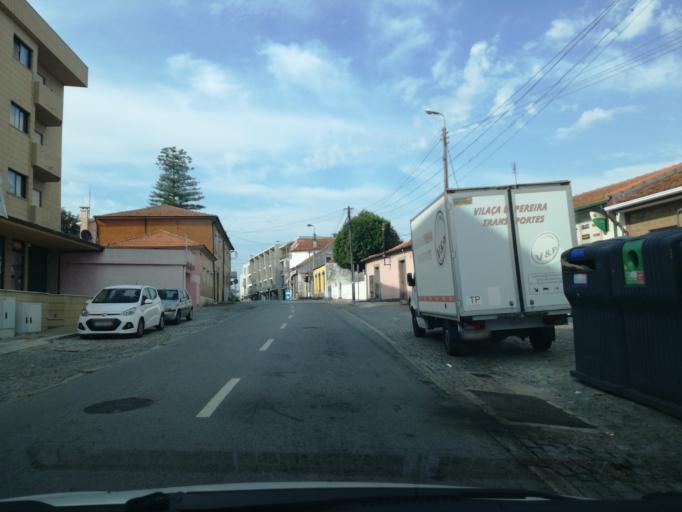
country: PT
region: Porto
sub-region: Vila Nova de Gaia
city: Sao Felix da Marinha
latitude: 41.0417
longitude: -8.6286
